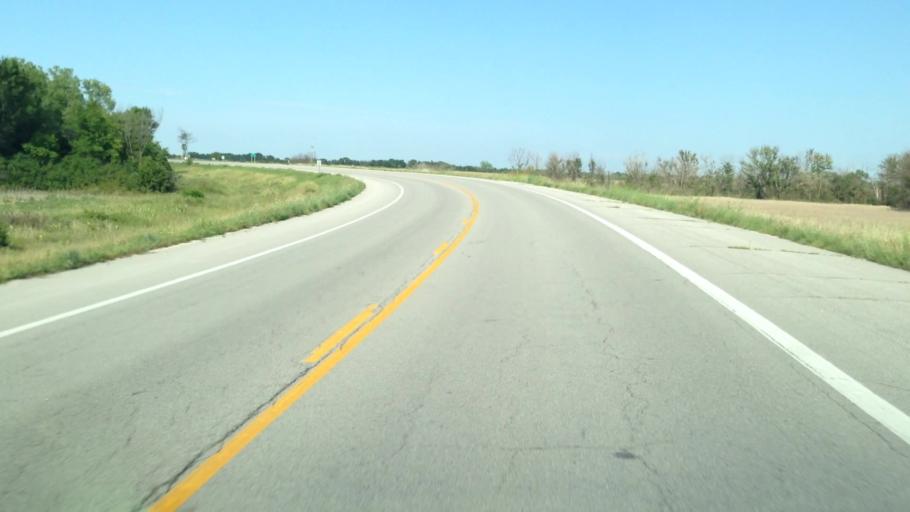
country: US
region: Kansas
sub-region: Neosho County
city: Erie
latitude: 37.6887
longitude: -95.1651
